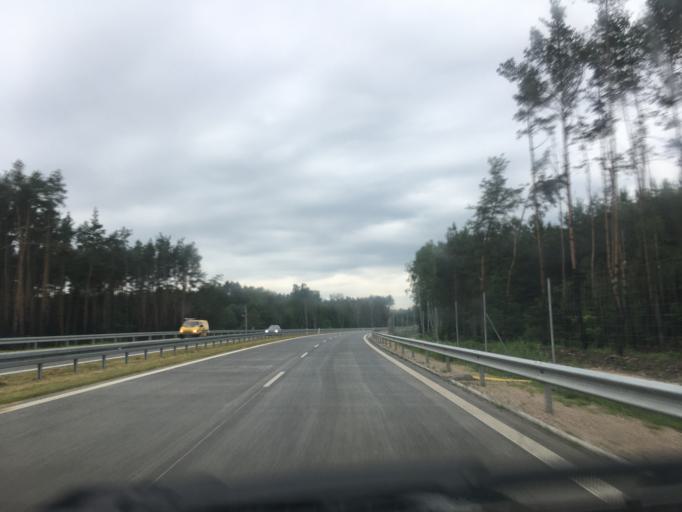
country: PL
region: Masovian Voivodeship
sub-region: Powiat piaseczynski
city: Gora Kalwaria
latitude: 51.9807
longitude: 21.1789
